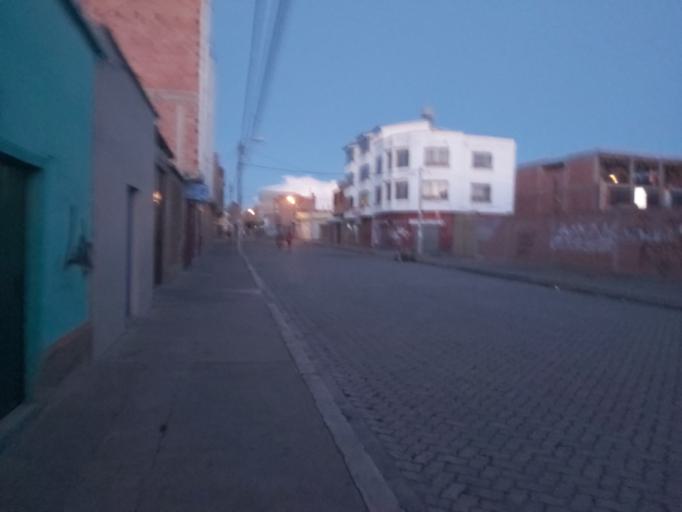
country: BO
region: La Paz
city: La Paz
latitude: -16.5287
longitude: -68.2001
